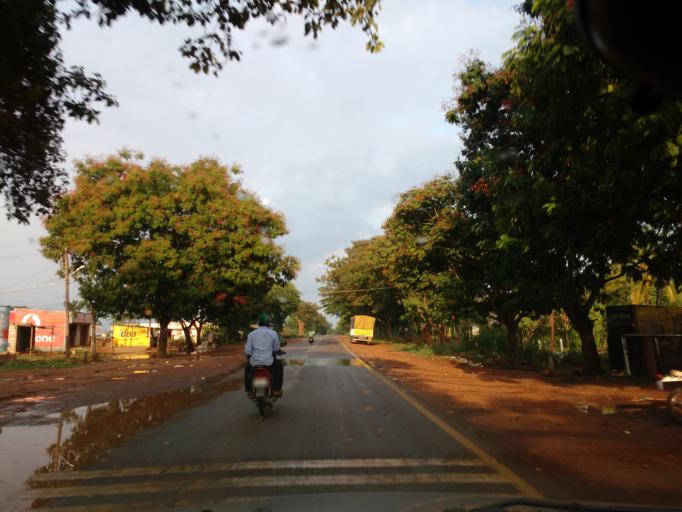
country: IN
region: Karnataka
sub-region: Tumkur
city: Tiptur
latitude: 13.2685
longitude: 76.3894
